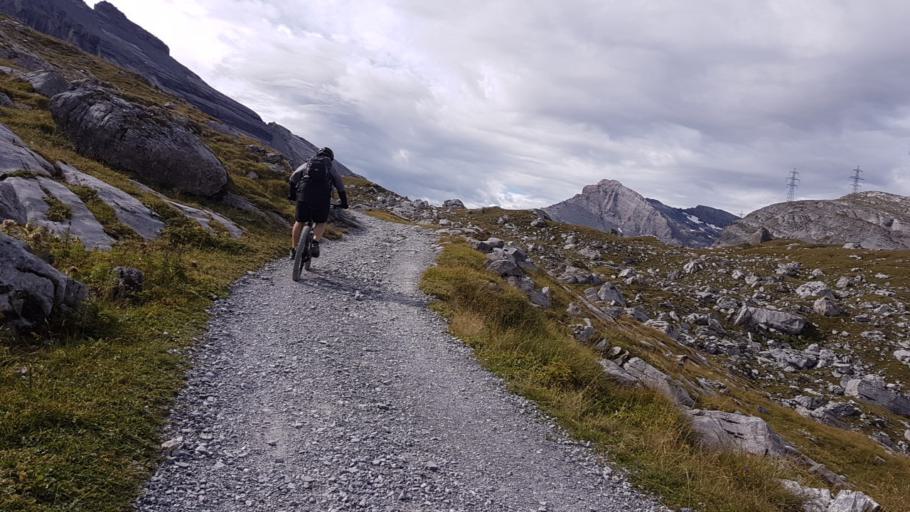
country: CH
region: Valais
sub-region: Leuk District
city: Leukerbad
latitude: 46.4214
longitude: 7.6233
